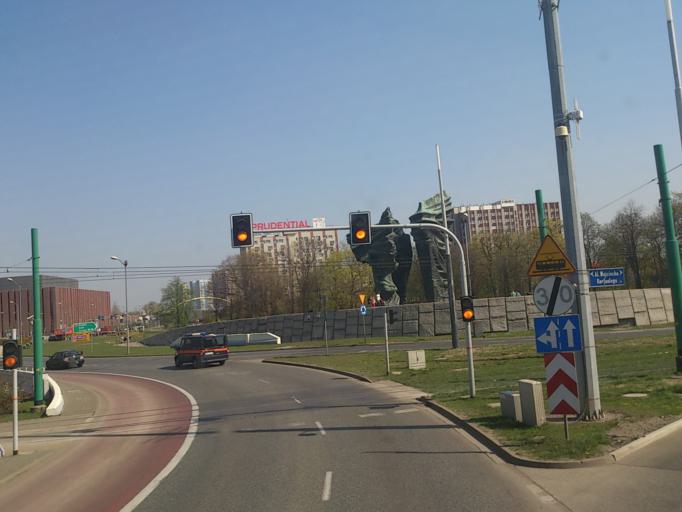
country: PL
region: Silesian Voivodeship
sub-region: Katowice
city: Katowice
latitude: 50.2640
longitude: 19.0230
